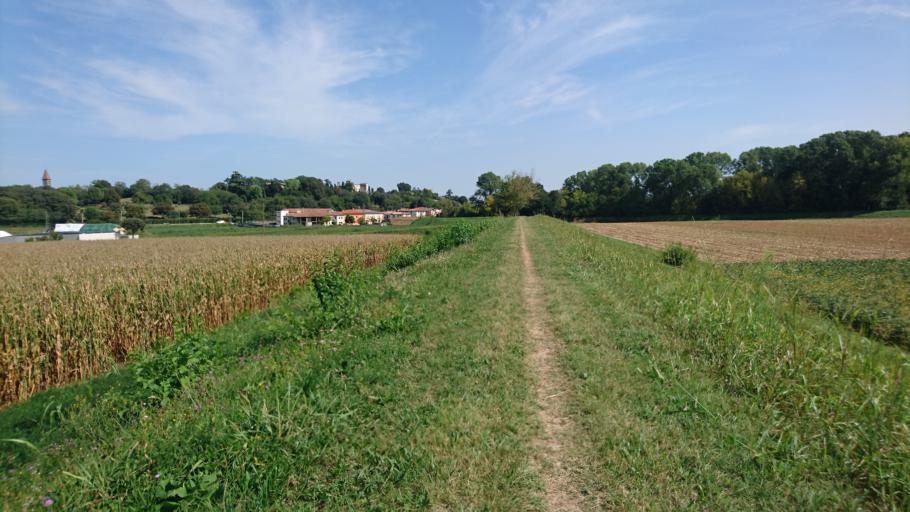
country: IT
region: Veneto
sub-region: Provincia di Vicenza
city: Montegalda
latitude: 45.4468
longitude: 11.6658
